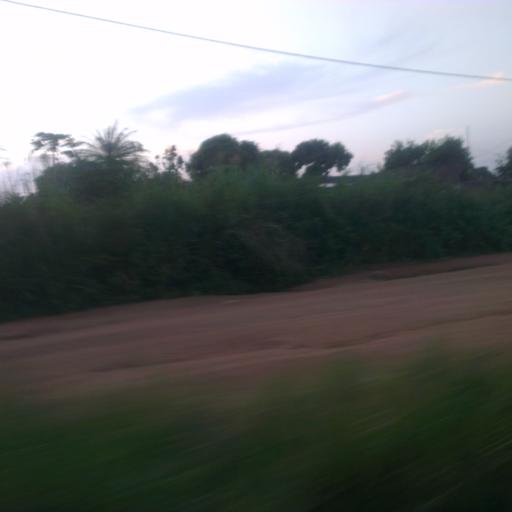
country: CI
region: Vallee du Bandama
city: Bouake
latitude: 7.6924
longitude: -5.0575
